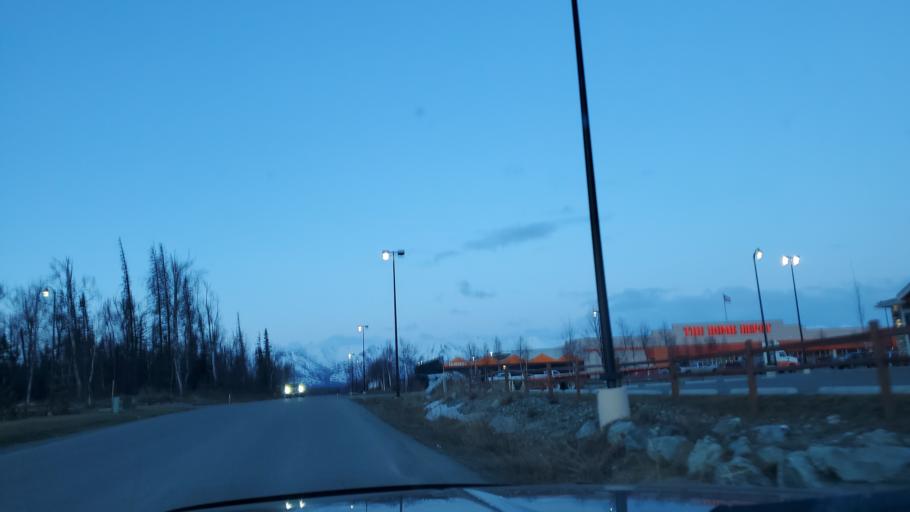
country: US
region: Alaska
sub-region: Matanuska-Susitna Borough
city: Wasilla
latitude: 61.5744
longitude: -149.4204
